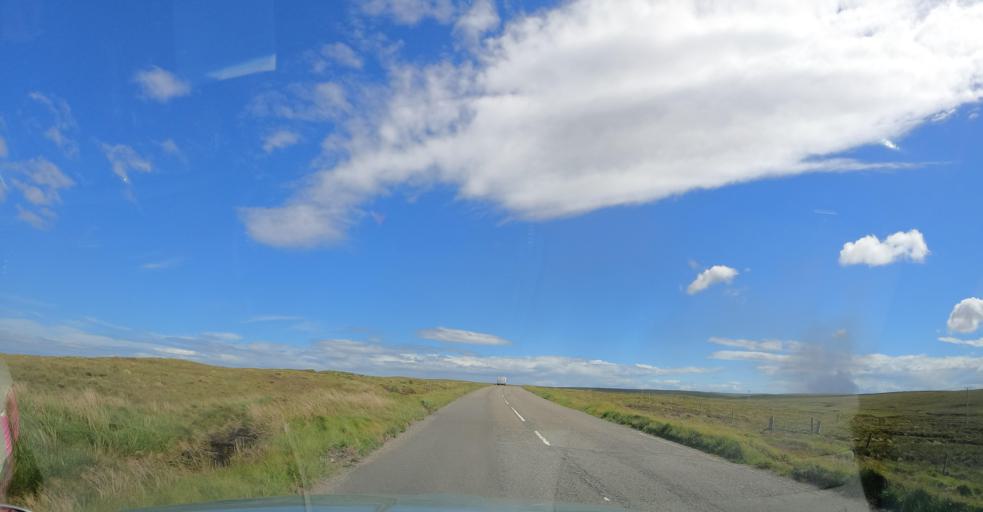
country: GB
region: Scotland
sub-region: Eilean Siar
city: Isle of Lewis
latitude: 58.3294
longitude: -6.4763
